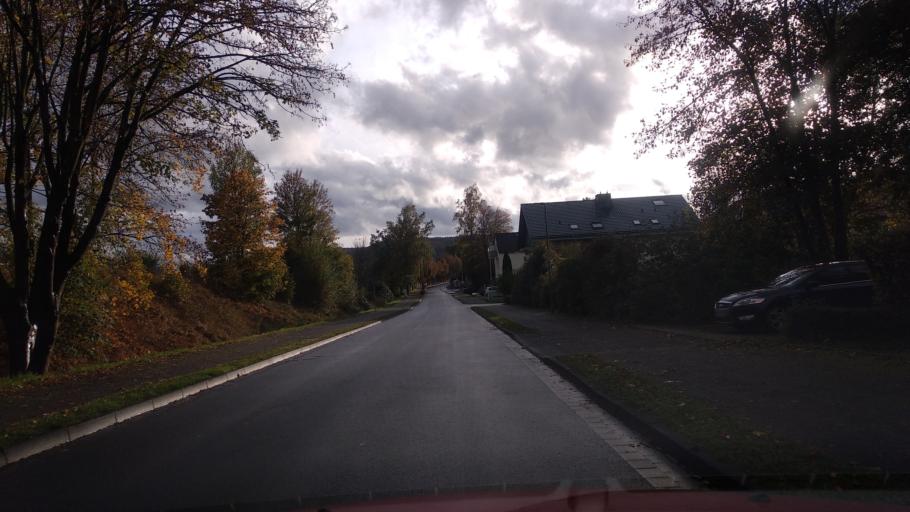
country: DE
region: North Rhine-Westphalia
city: Beverungen
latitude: 51.6687
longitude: 9.3702
